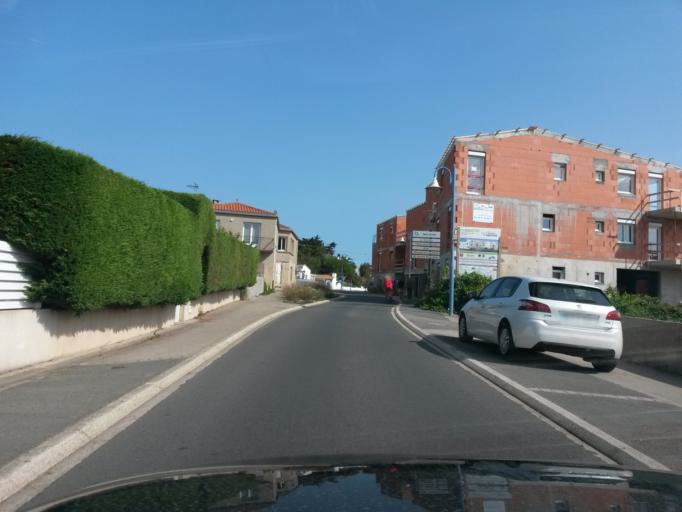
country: FR
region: Pays de la Loire
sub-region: Departement de la Vendee
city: Bretignolles-sur-Mer
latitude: 46.6038
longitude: -1.8309
